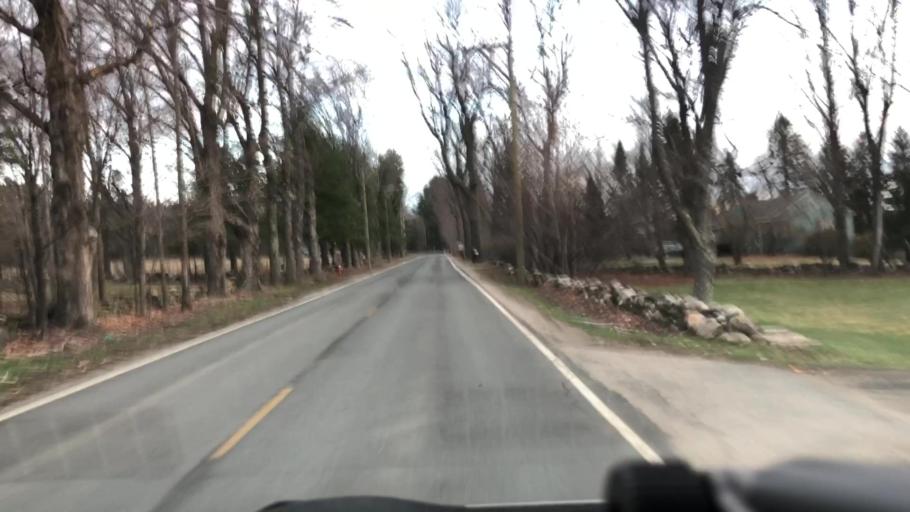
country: US
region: Massachusetts
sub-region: Hampshire County
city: Chesterfield
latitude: 42.4187
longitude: -72.9408
